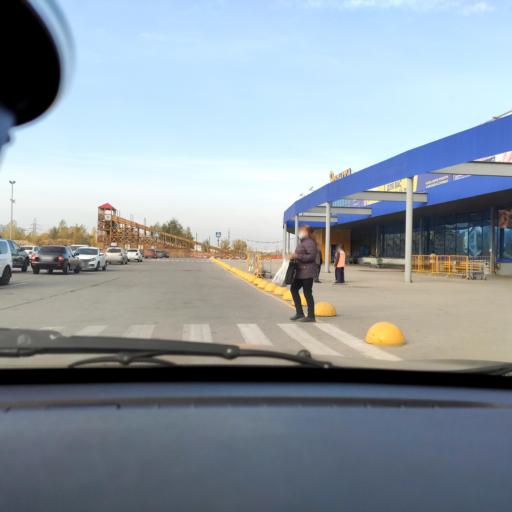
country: RU
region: Samara
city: Tol'yatti
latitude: 53.5485
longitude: 49.3604
